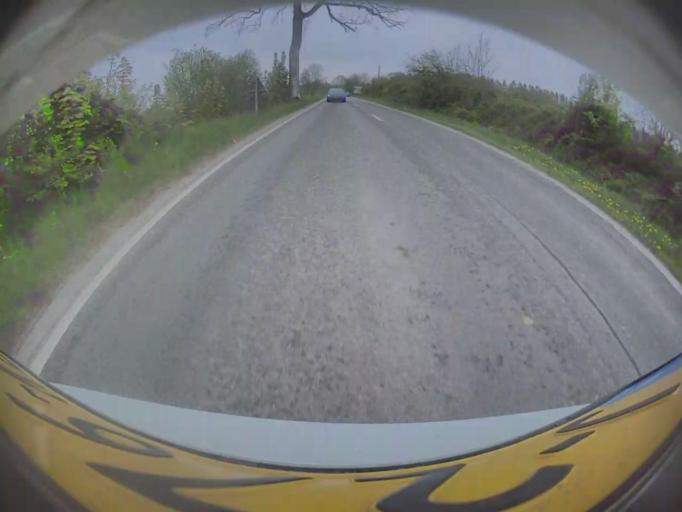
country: BE
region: Wallonia
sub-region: Province de Liege
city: Hamoir
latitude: 50.4233
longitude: 5.5747
